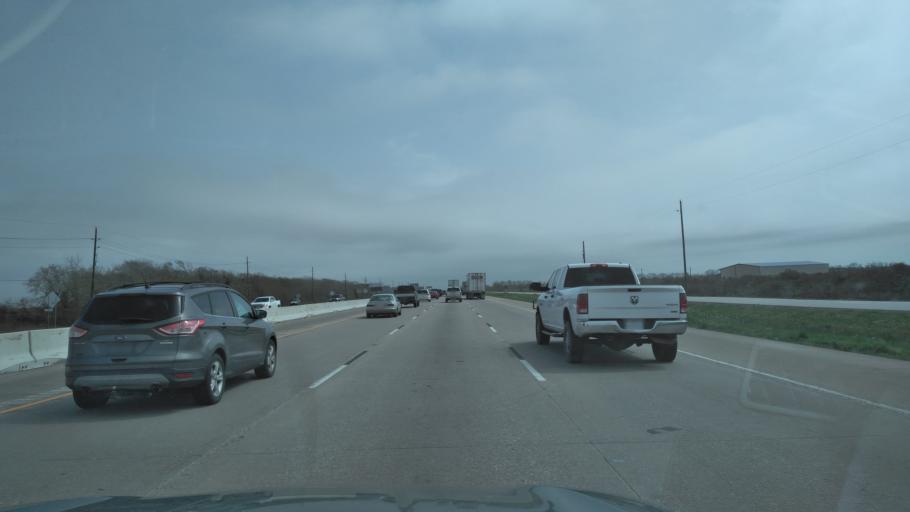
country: US
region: Texas
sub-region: Chambers County
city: Old River-Winfree
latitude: 29.8268
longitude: -94.8365
